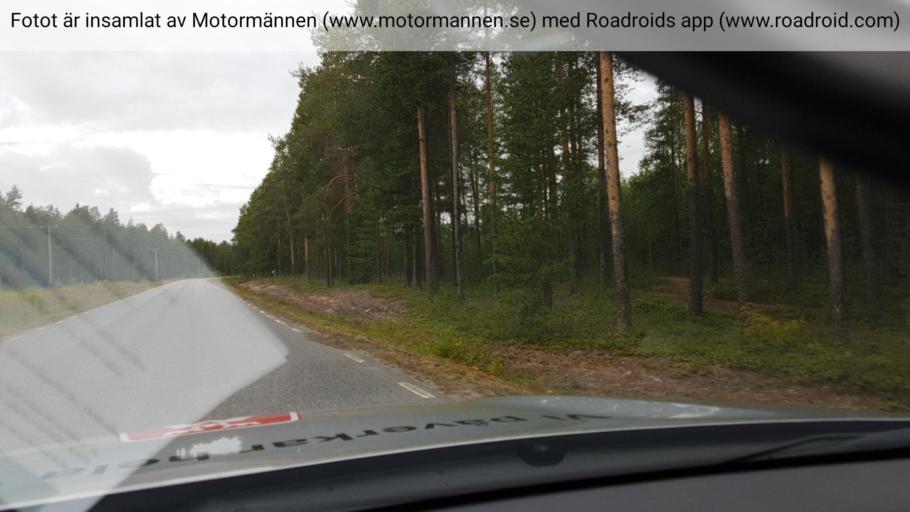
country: SE
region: Norrbotten
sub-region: Bodens Kommun
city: Boden
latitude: 65.8152
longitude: 21.6034
